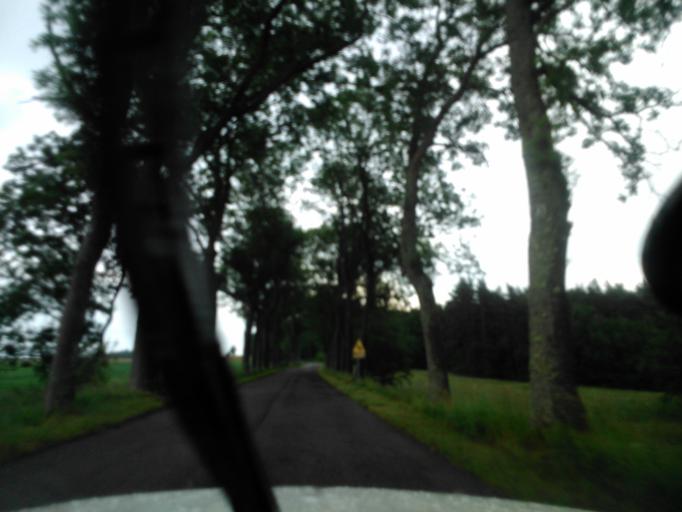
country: PL
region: Pomeranian Voivodeship
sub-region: Powiat slupski
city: Smoldzino
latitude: 54.6539
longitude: 17.2385
